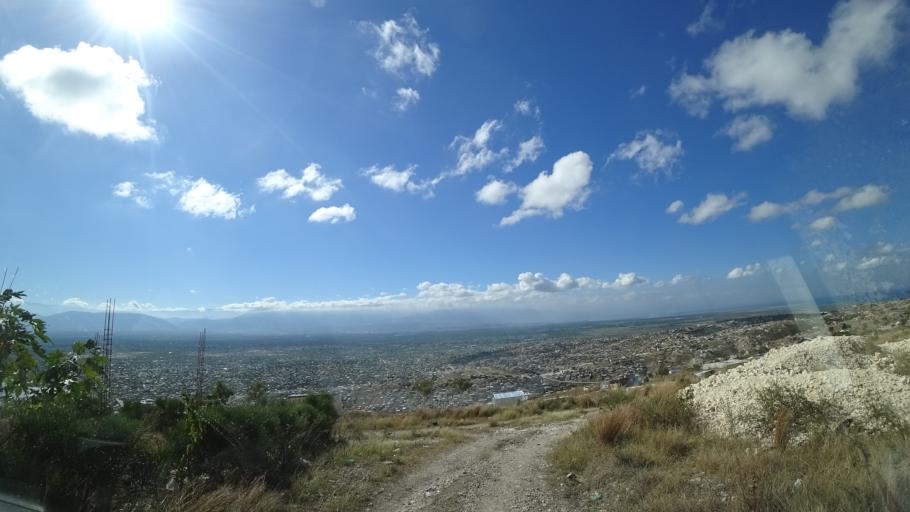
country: HT
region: Ouest
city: Croix des Bouquets
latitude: 18.6725
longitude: -72.2599
